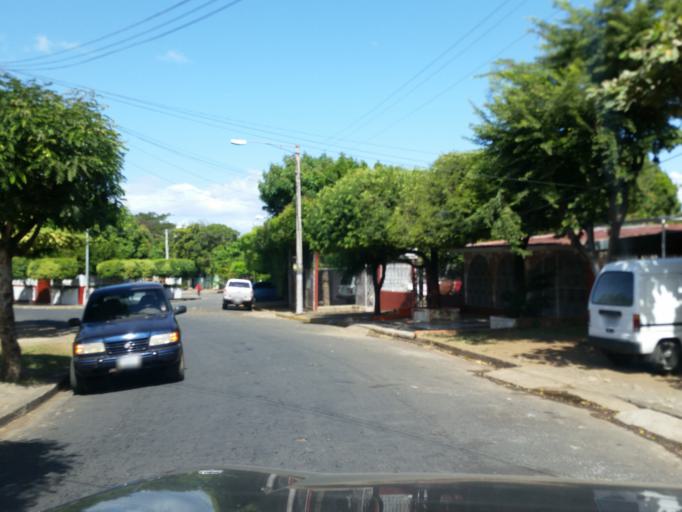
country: NI
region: Managua
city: Managua
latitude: 12.1195
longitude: -86.2380
